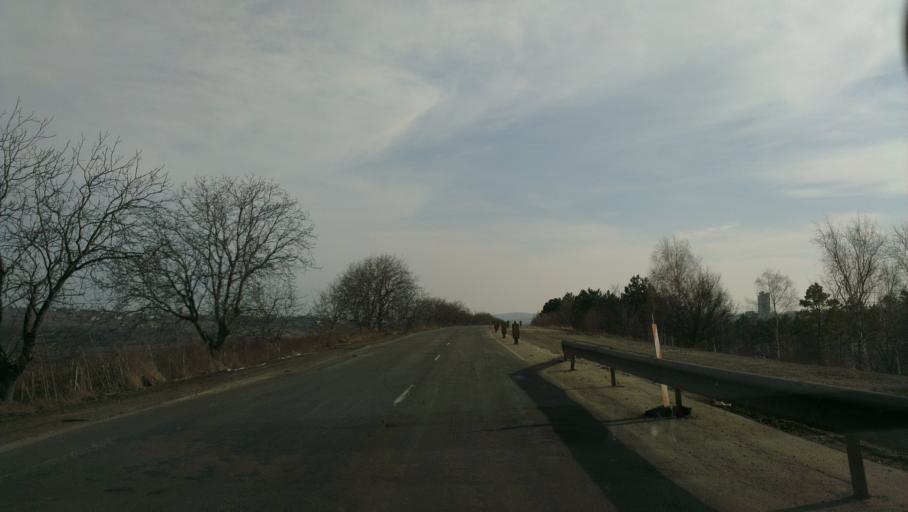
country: MD
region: Laloveni
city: Ialoveni
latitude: 46.9865
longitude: 28.7439
